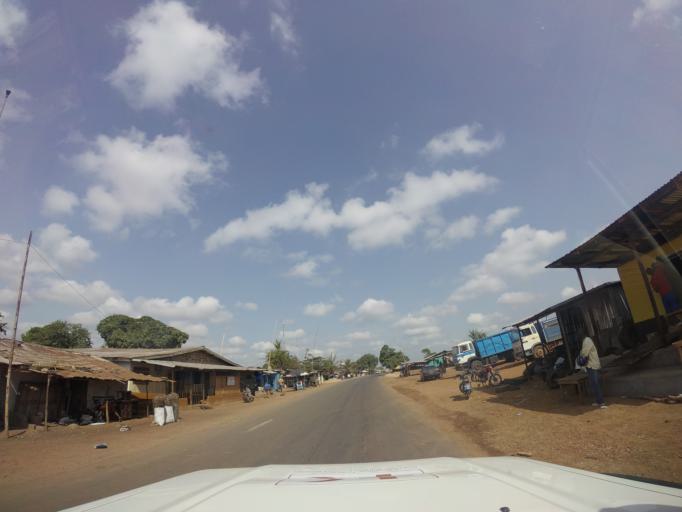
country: LR
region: Bomi
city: Tubmanburg
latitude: 6.7134
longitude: -10.9701
